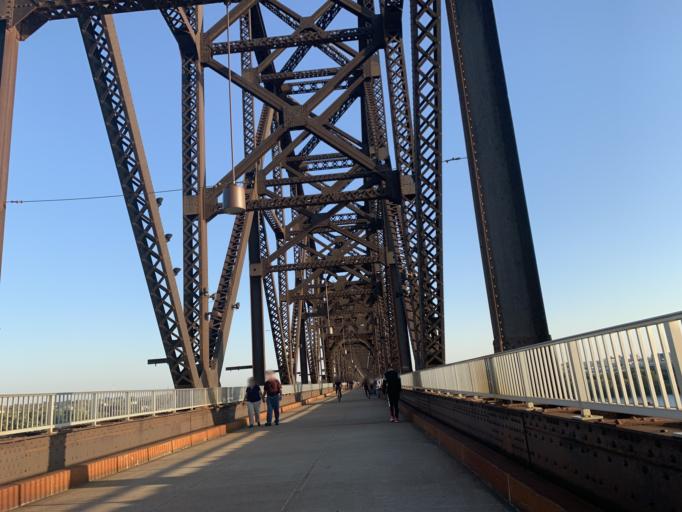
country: US
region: Indiana
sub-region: Clark County
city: Jeffersonville
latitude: 38.2672
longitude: -85.7402
